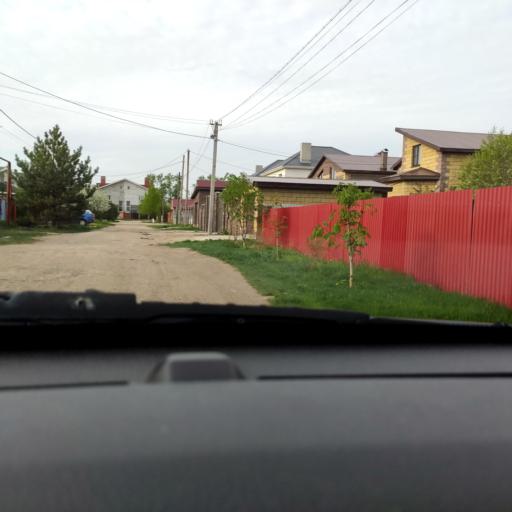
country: RU
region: Samara
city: Tol'yatti
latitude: 53.5632
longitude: 49.3765
